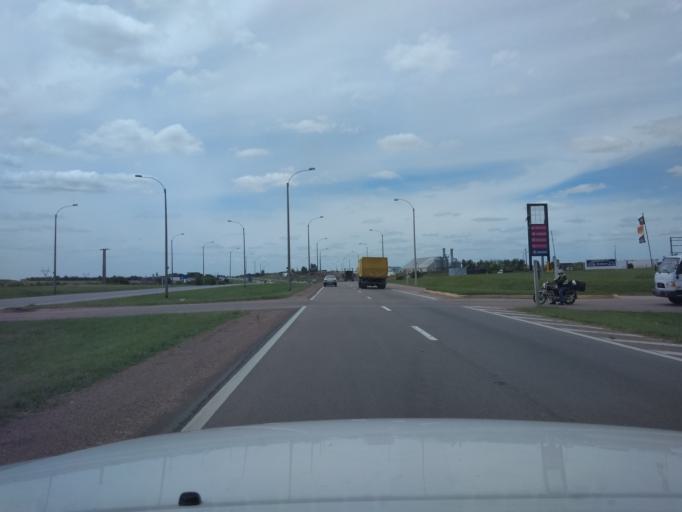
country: UY
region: Canelones
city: La Paz
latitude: -34.7505
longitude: -56.2553
